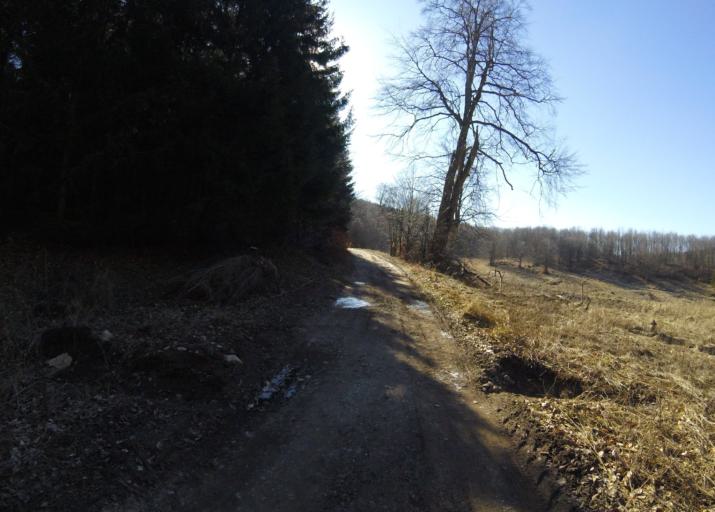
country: HU
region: Heves
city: Szilvasvarad
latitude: 48.0865
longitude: 20.4739
